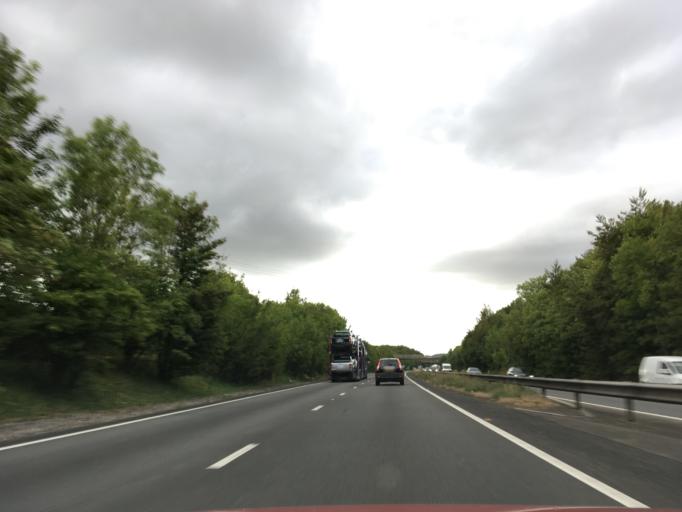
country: GB
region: England
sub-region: Hampshire
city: Kings Worthy
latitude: 51.1472
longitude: -1.3475
